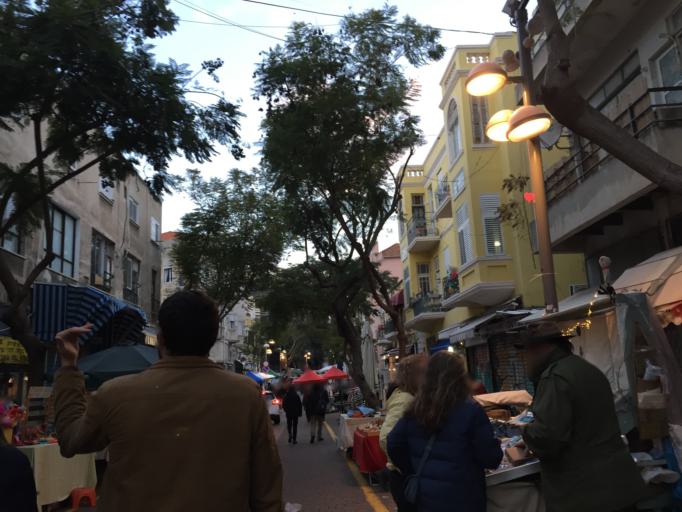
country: IL
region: Tel Aviv
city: Tel Aviv
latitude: 32.0679
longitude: 34.7701
